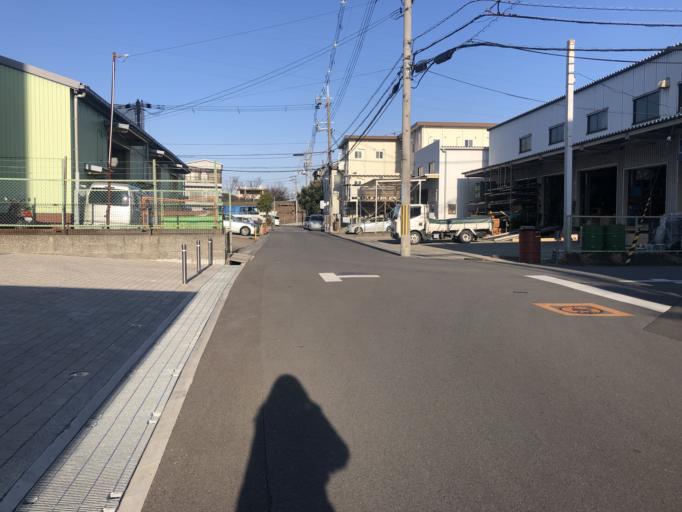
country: JP
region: Osaka
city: Suita
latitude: 34.7512
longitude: 135.5120
